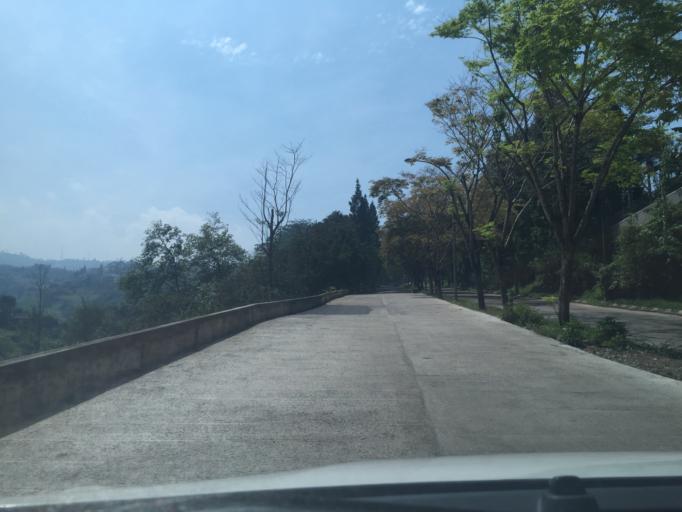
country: ID
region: West Java
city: Bandung
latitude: -6.8648
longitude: 107.6390
